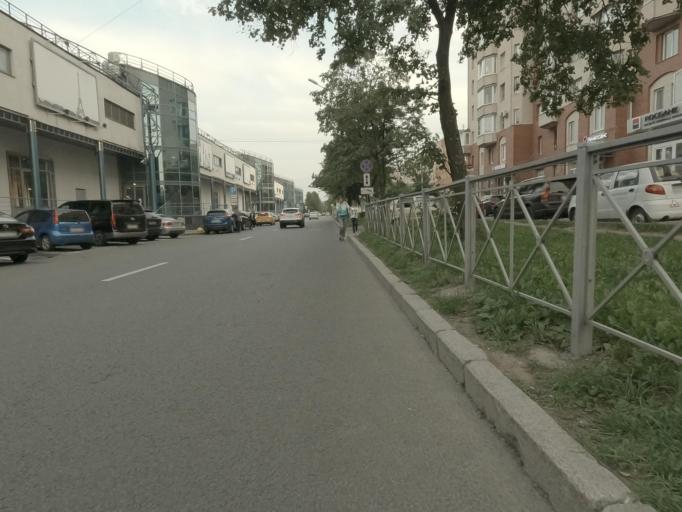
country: RU
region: St.-Petersburg
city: Dachnoye
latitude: 59.8509
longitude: 30.2678
